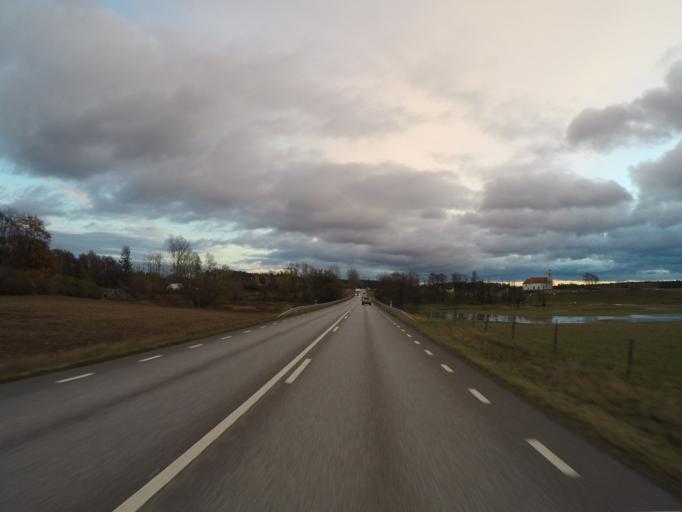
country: SE
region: Skane
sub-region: Kristianstads Kommun
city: Norra Asum
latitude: 55.9390
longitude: 14.0718
